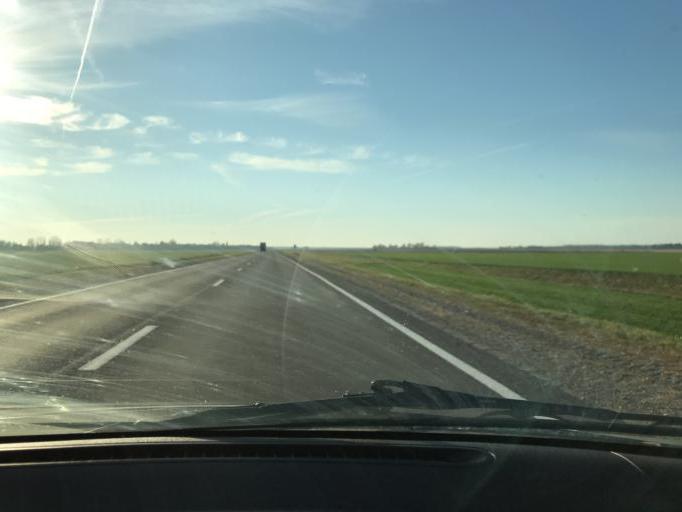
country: BY
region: Brest
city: Antopal'
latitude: 52.2086
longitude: 24.6236
